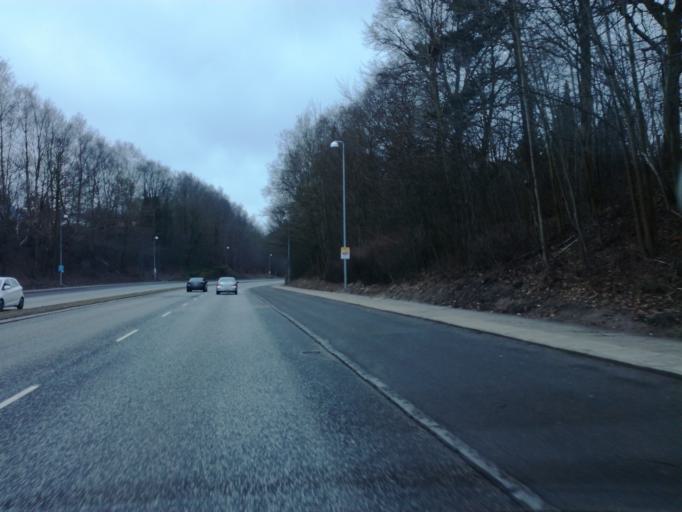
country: DK
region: South Denmark
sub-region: Vejle Kommune
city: Vejle
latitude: 55.7171
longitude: 9.5549
